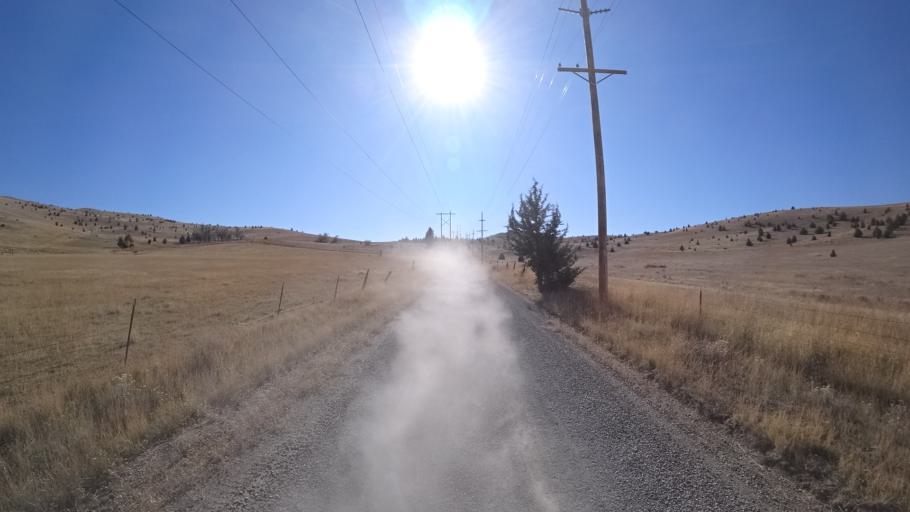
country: US
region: California
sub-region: Siskiyou County
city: Montague
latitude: 41.7807
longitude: -122.3590
